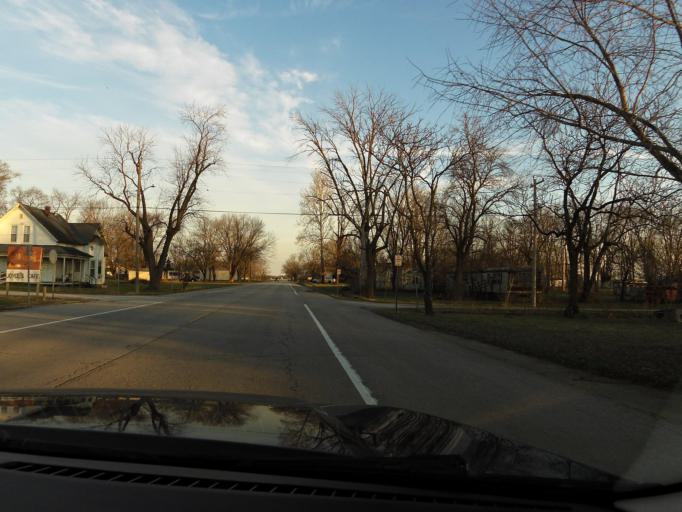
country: US
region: Illinois
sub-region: Fayette County
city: Vandalia
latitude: 38.8023
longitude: -89.0864
